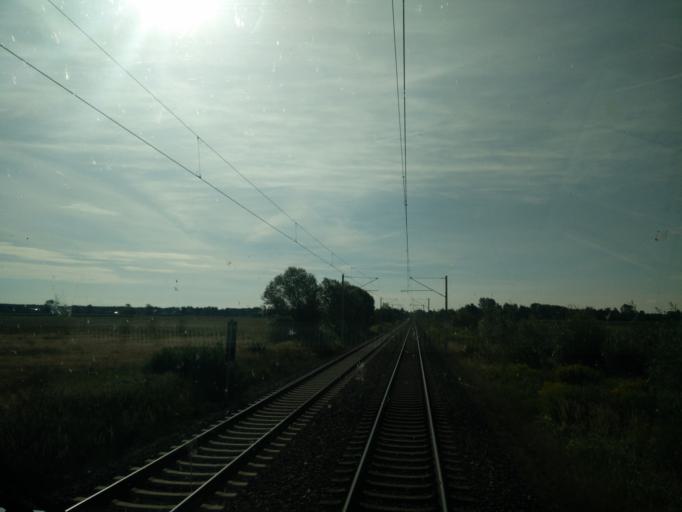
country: DE
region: Brandenburg
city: Luebben
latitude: 51.9679
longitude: 13.8129
